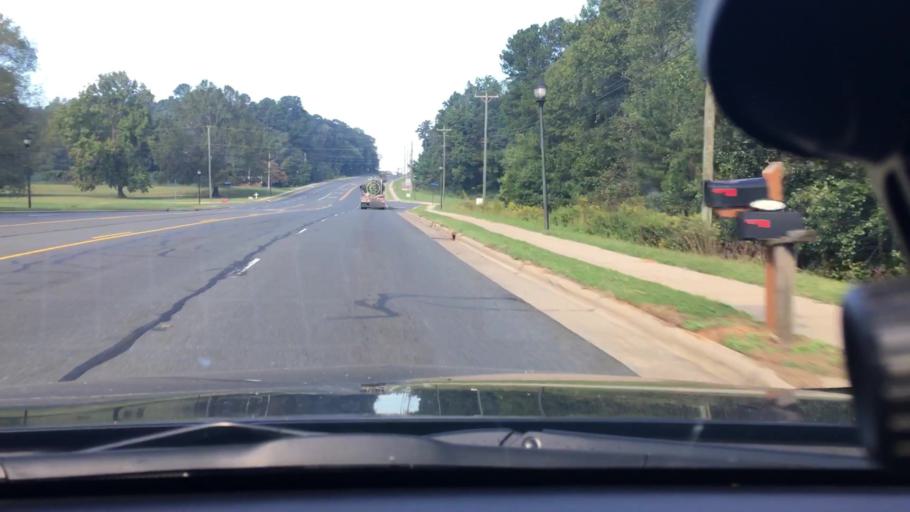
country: US
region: North Carolina
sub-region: Stanly County
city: Locust
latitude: 35.2603
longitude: -80.4037
